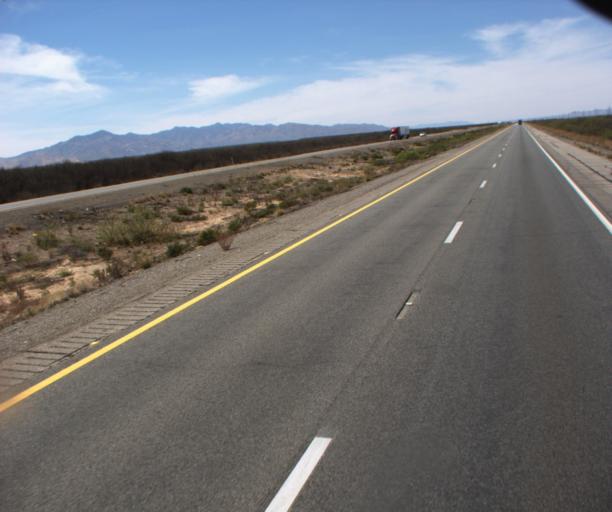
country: US
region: Arizona
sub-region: Cochise County
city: Willcox
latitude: 32.2823
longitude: -109.2877
